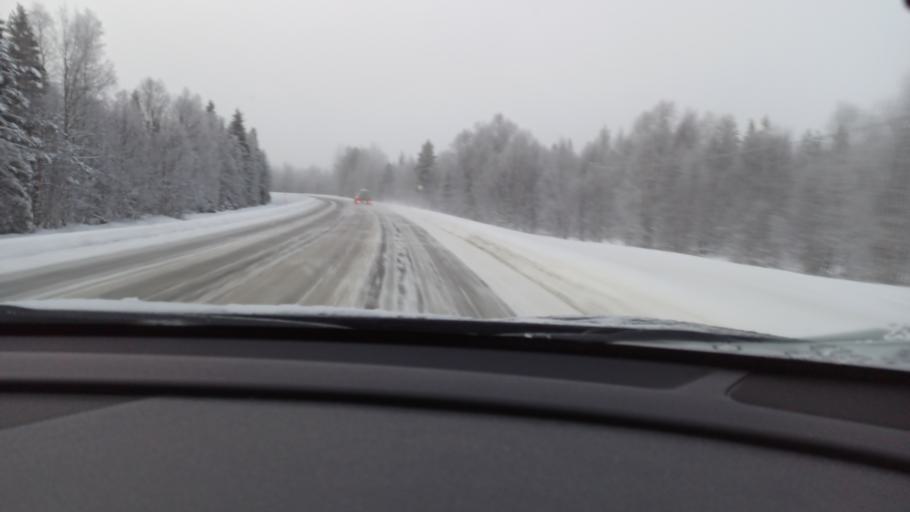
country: FI
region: Lapland
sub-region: Pohjois-Lappi
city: Sodankylae
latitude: 66.9259
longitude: 26.2100
